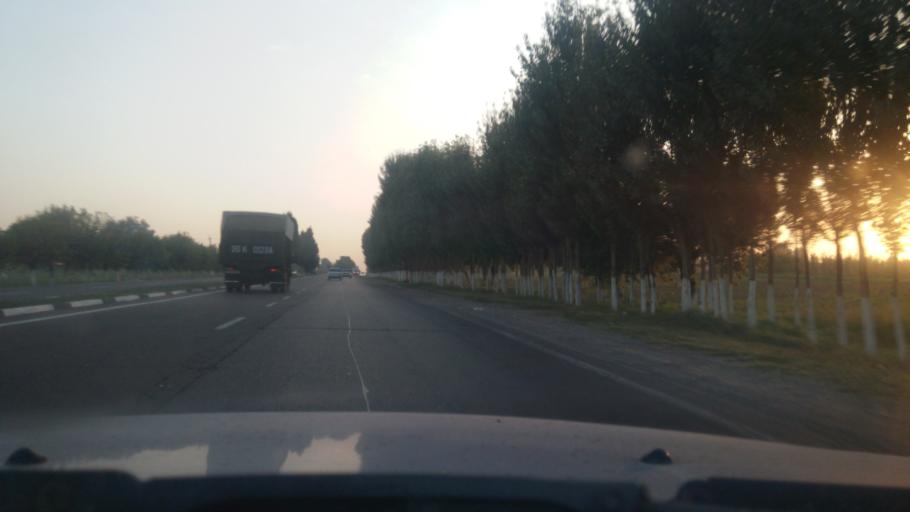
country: UZ
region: Toshkent
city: Yangiyul
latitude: 41.1157
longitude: 68.9877
